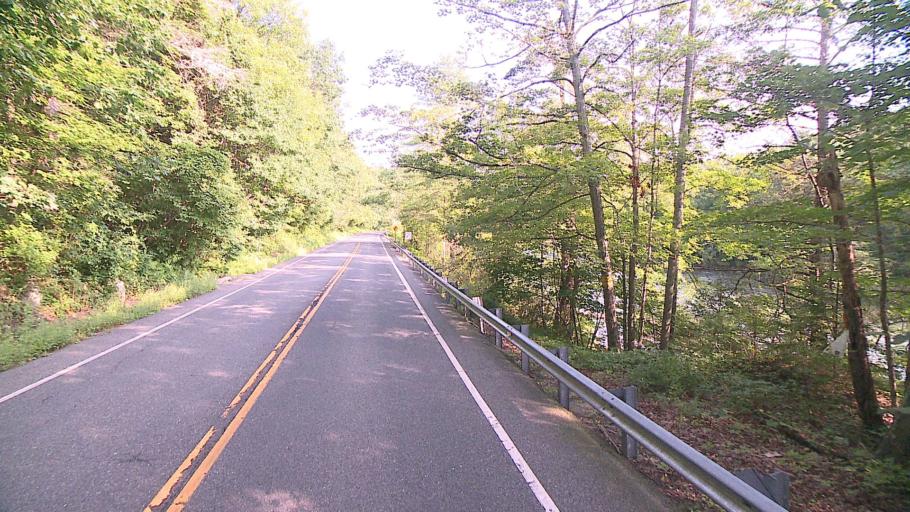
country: US
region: Connecticut
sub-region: Litchfield County
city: Kent
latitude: 41.8485
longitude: -73.3752
